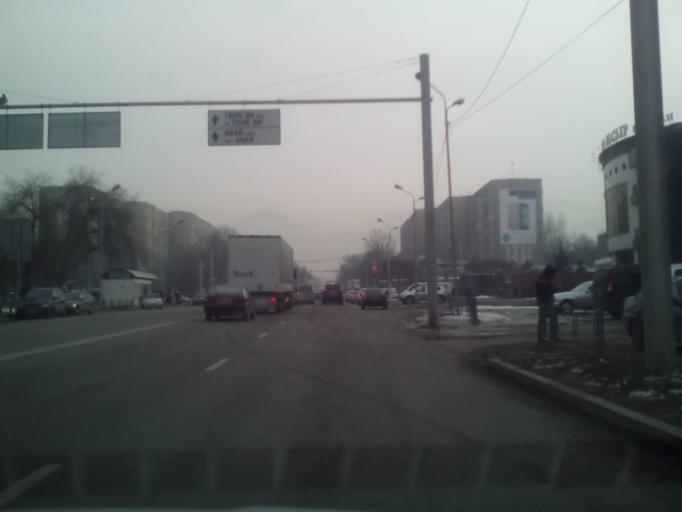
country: KZ
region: Almaty Qalasy
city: Almaty
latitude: 43.2405
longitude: 76.8288
